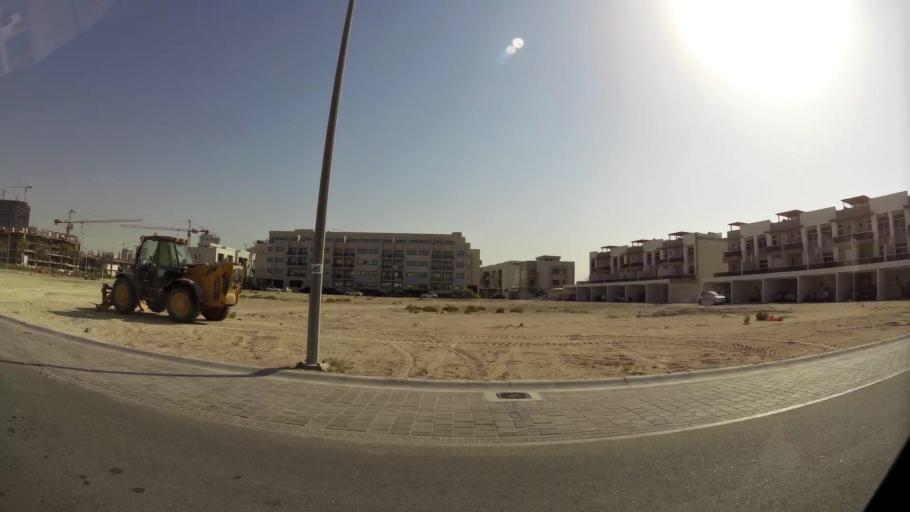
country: AE
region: Dubai
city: Dubai
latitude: 25.0642
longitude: 55.2039
